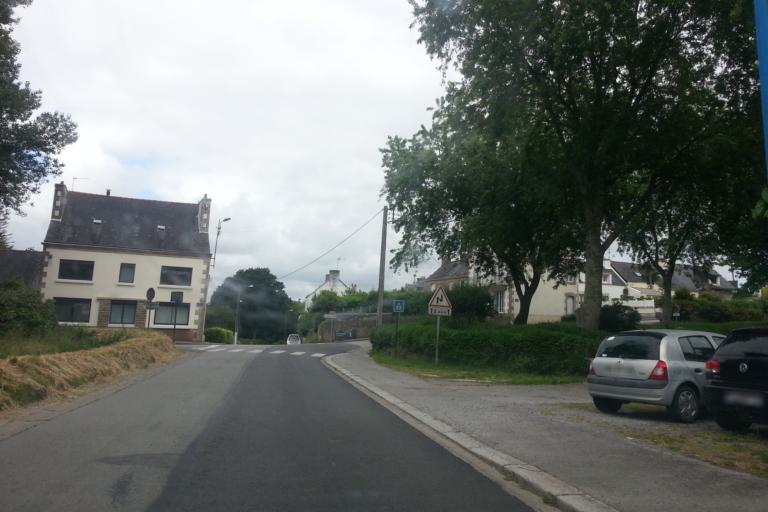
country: FR
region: Brittany
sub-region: Departement du Finistere
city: Elliant
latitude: 47.9978
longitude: -3.8896
